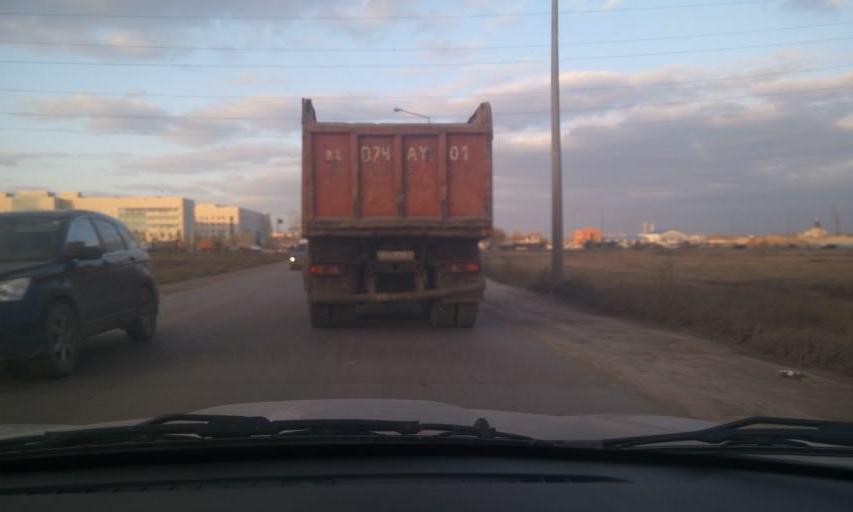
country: KZ
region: Astana Qalasy
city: Astana
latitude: 51.1364
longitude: 71.5270
